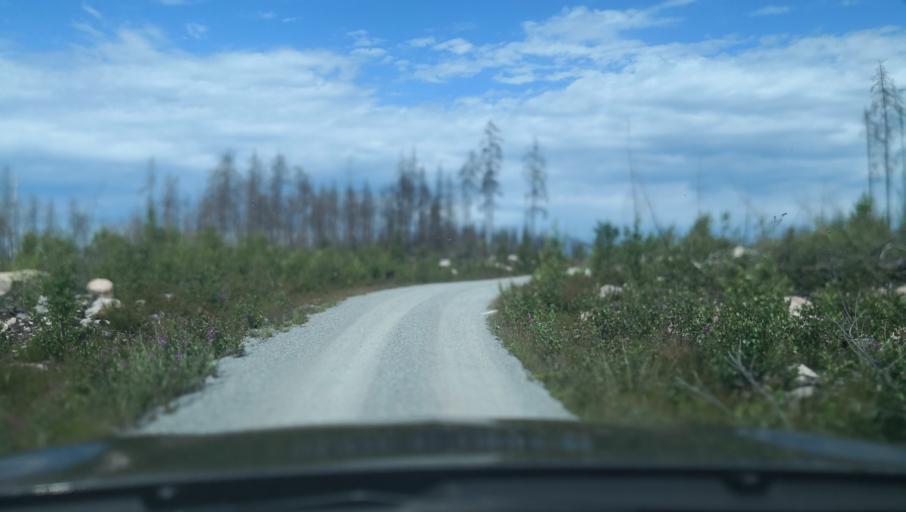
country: SE
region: Vaestmanland
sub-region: Surahammars Kommun
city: Ramnas
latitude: 59.9196
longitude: 16.1610
